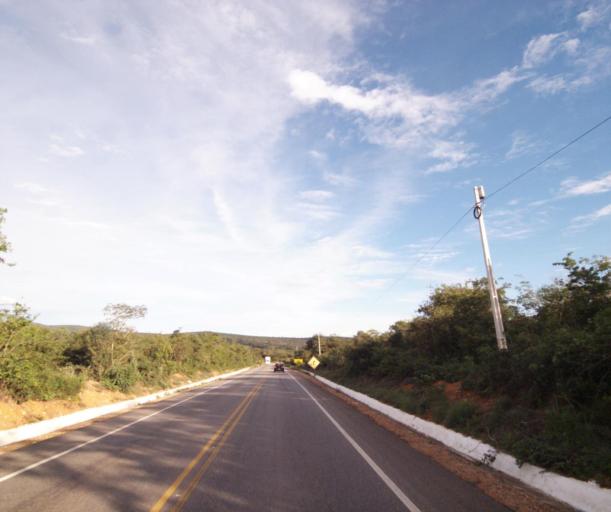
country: BR
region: Bahia
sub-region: Caetite
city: Caetite
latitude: -14.1282
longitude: -42.4144
